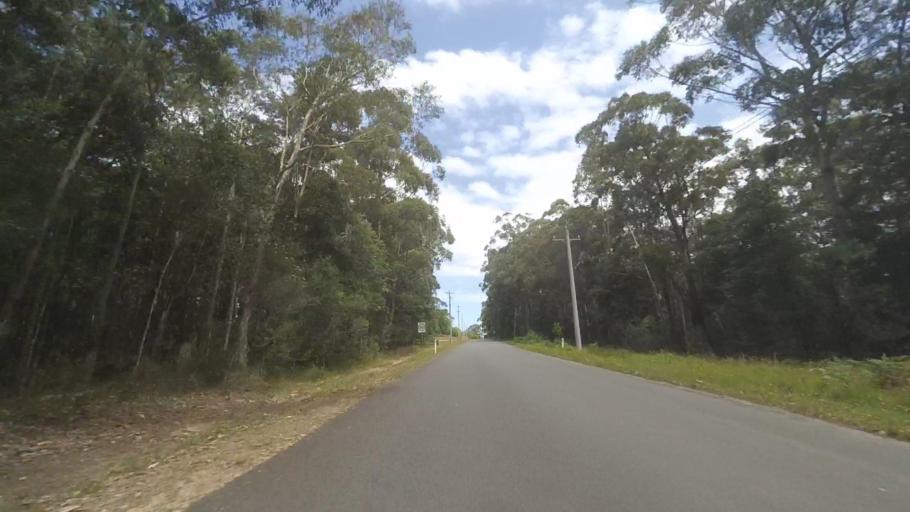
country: AU
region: New South Wales
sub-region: Shoalhaven Shire
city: Milton
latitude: -35.3936
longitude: 150.3690
